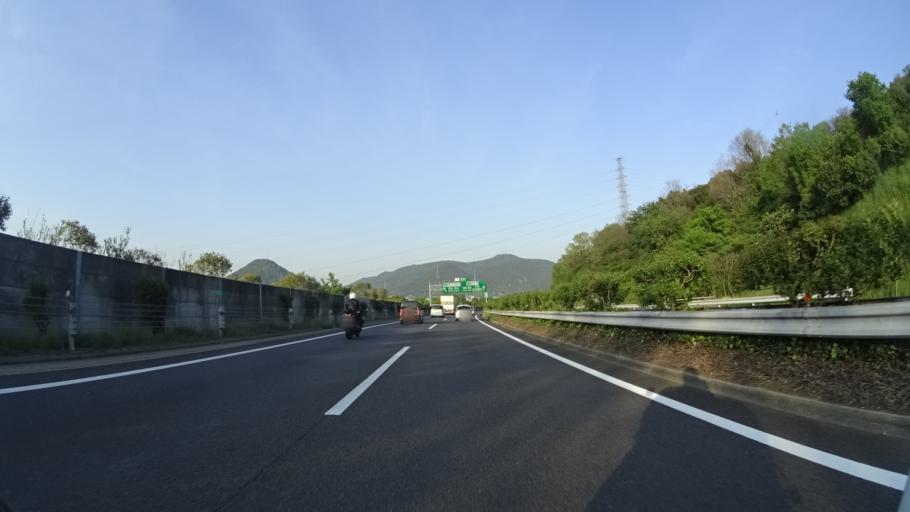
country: JP
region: Kagawa
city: Sakaidecho
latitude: 34.2814
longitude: 133.8432
